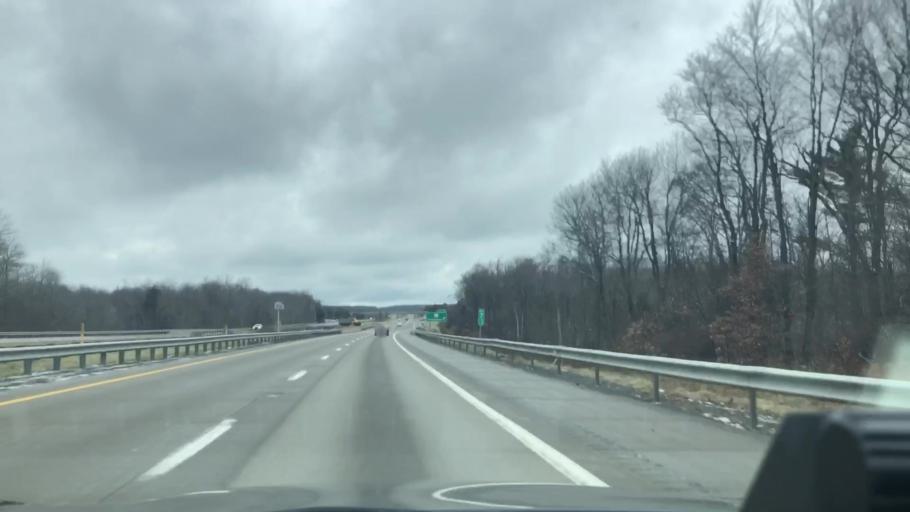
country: US
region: Pennsylvania
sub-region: Monroe County
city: Pocono Pines
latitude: 41.1669
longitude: -75.4235
